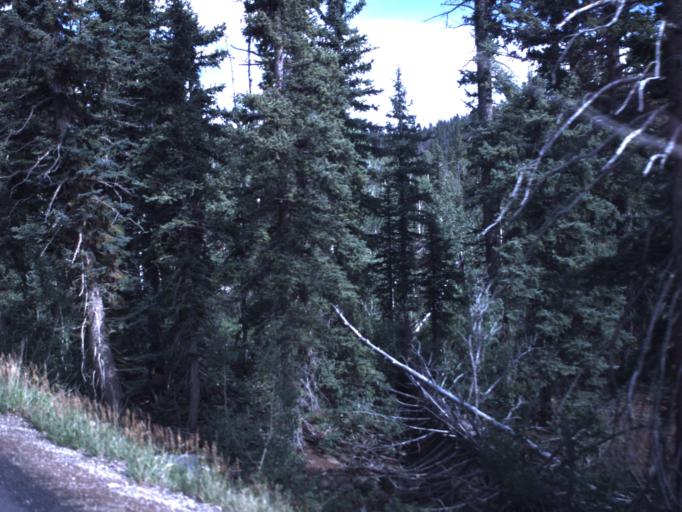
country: US
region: Utah
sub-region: Iron County
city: Parowan
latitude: 37.5177
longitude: -112.7018
